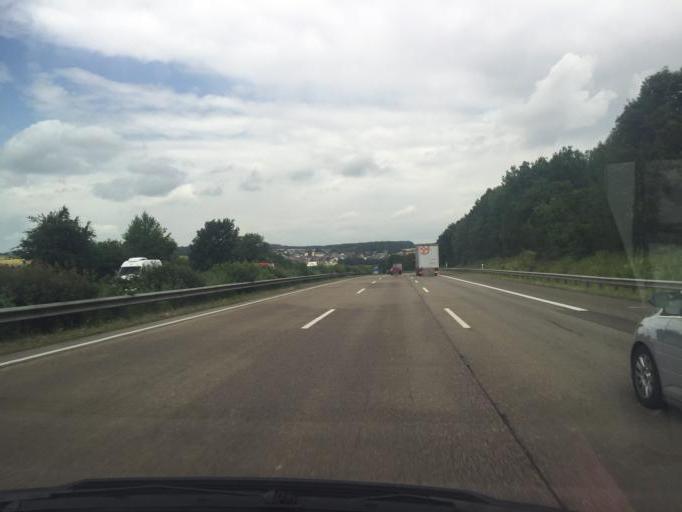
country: DE
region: Rheinland-Pfalz
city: Nomborn
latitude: 50.4381
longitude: 7.9176
